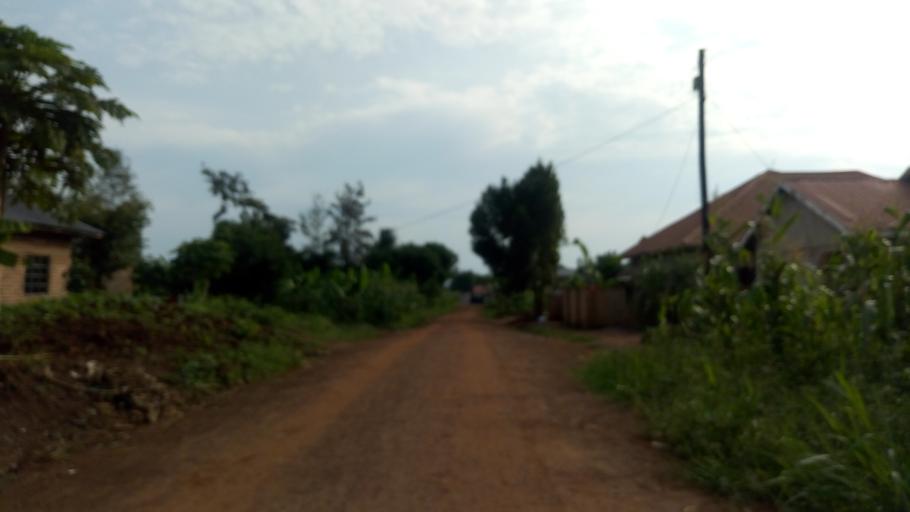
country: UG
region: Western Region
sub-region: Kiryandongo District
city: Kiryandongo
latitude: 1.8039
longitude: 32.0070
